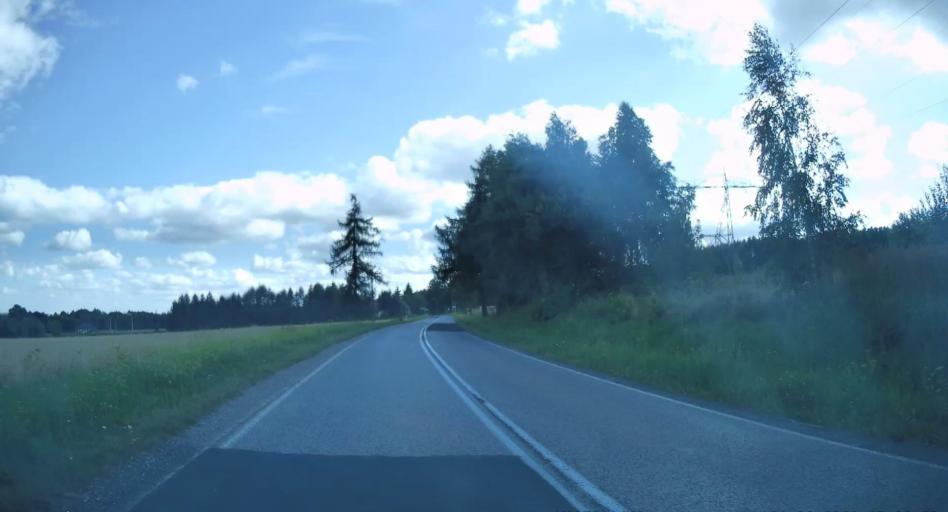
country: PL
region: Swietokrzyskie
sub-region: Powiat kielecki
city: Lagow
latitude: 50.8111
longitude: 21.0797
